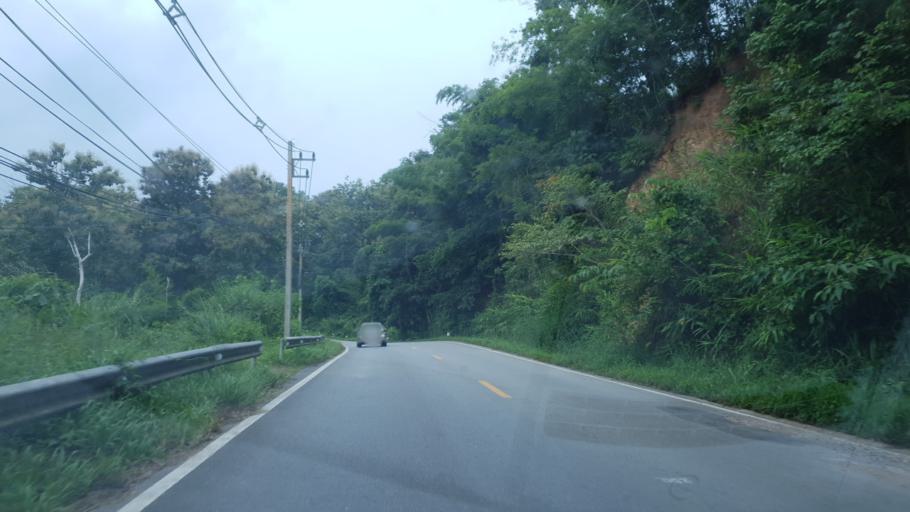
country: TH
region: Mae Hong Son
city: Khun Yuam
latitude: 18.7154
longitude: 97.9087
